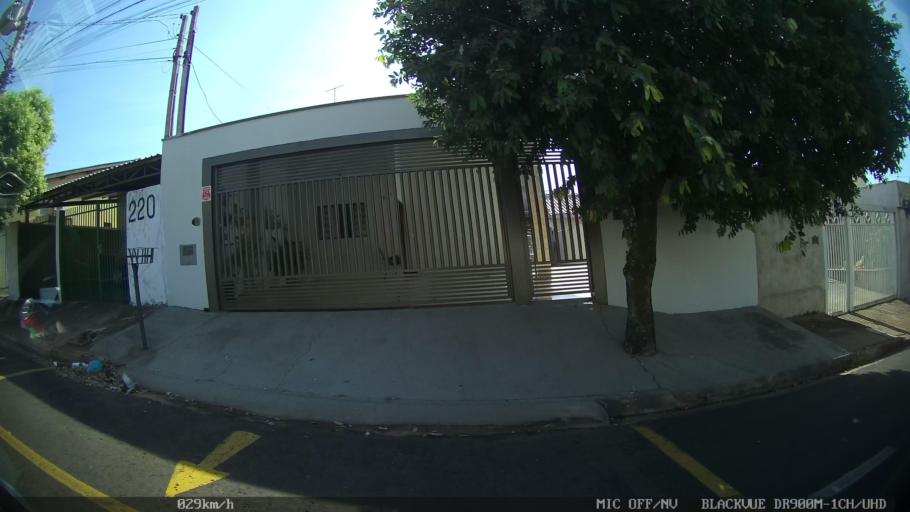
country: BR
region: Sao Paulo
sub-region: Sao Jose Do Rio Preto
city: Sao Jose do Rio Preto
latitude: -20.7864
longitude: -49.4309
